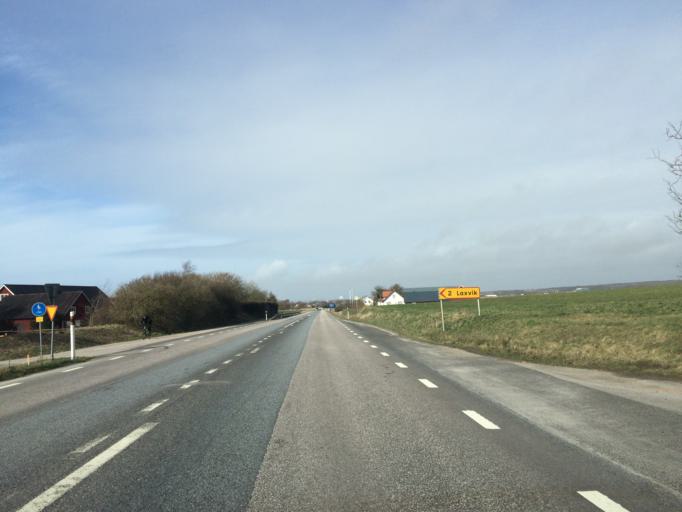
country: SE
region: Halland
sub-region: Halmstads Kommun
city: Paarp
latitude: 56.6050
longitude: 12.9607
